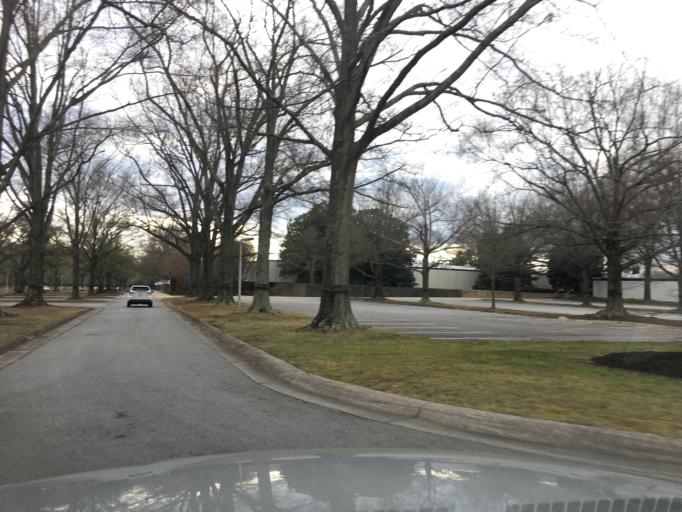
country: US
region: South Carolina
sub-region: Spartanburg County
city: Saxon
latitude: 34.9886
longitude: -81.9554
